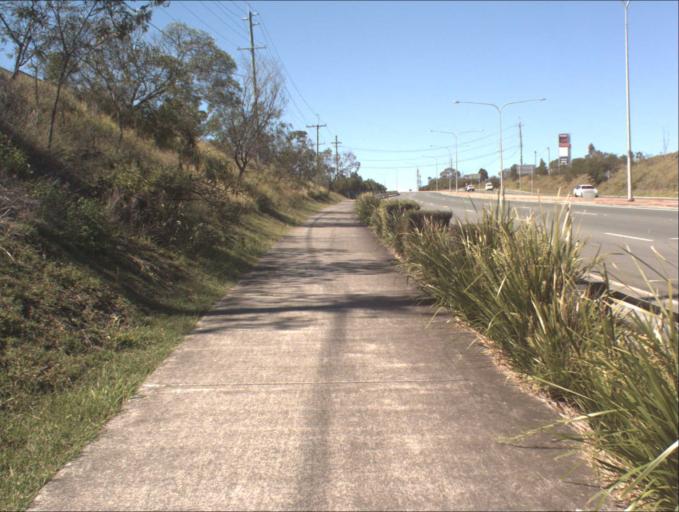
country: AU
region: Queensland
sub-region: Logan
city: Waterford West
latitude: -27.7033
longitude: 153.1597
